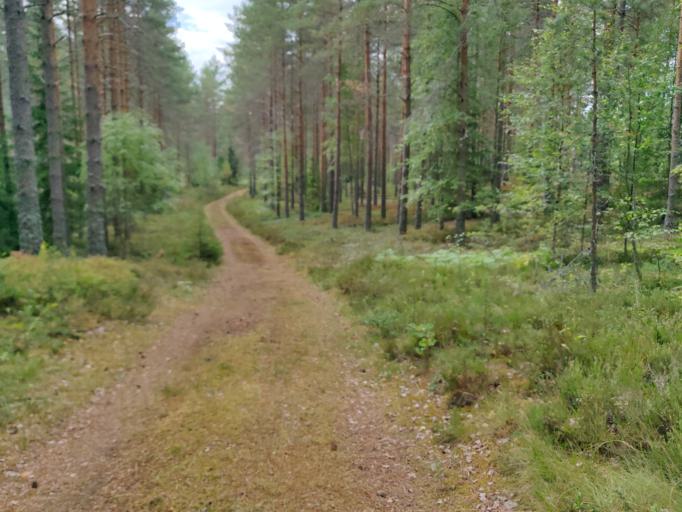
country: SE
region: Vaermland
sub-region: Munkfors Kommun
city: Munkfors
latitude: 59.9658
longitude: 13.5492
